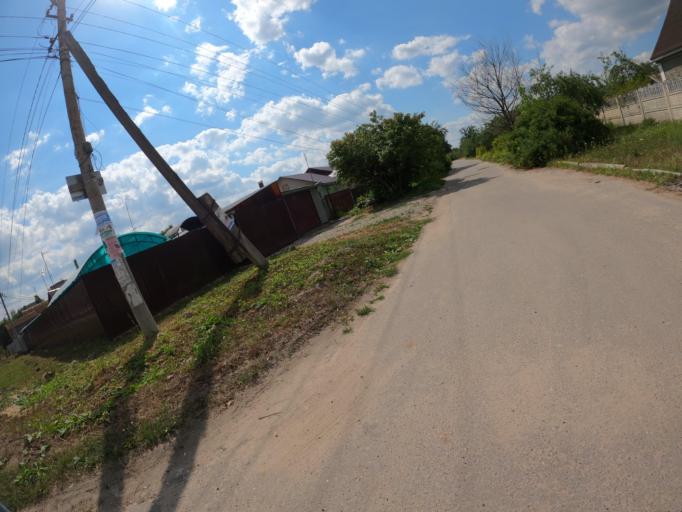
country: RU
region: Moskovskaya
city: Peski
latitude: 55.2784
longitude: 38.7485
